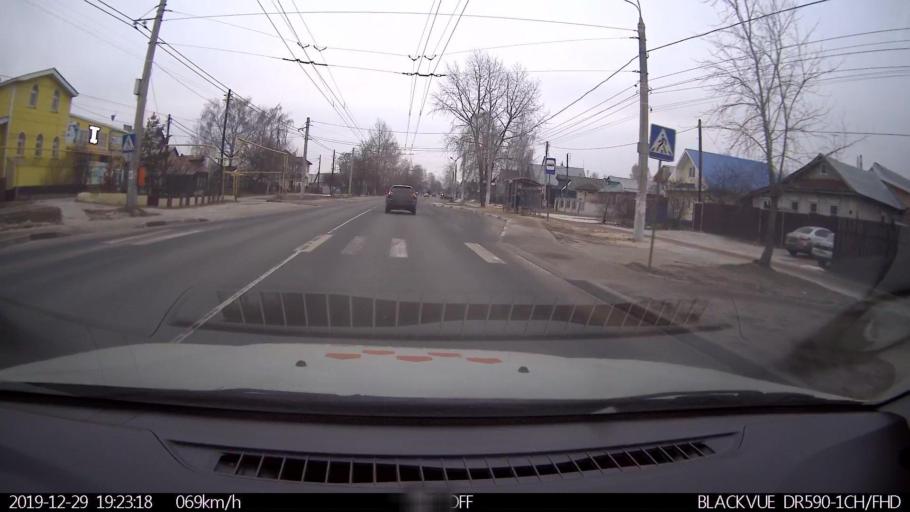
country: RU
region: Nizjnij Novgorod
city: Gorbatovka
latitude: 56.3815
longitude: 43.8038
